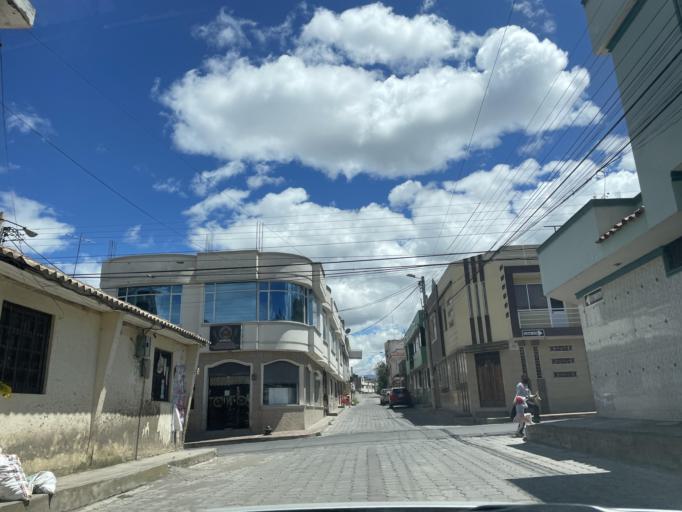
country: EC
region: Chimborazo
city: Guano
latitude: -1.6050
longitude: -78.6450
